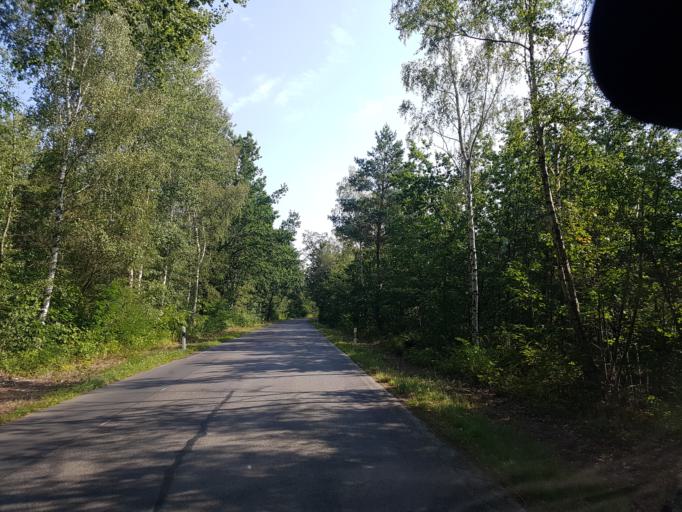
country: DE
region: Brandenburg
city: Lauchhammer
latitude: 51.5141
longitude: 13.7415
